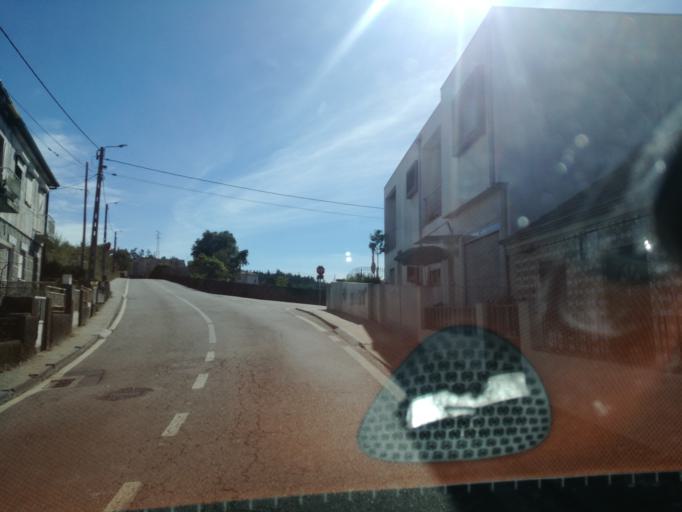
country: PT
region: Braga
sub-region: Guimaraes
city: Guimaraes
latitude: 41.4603
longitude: -8.2922
